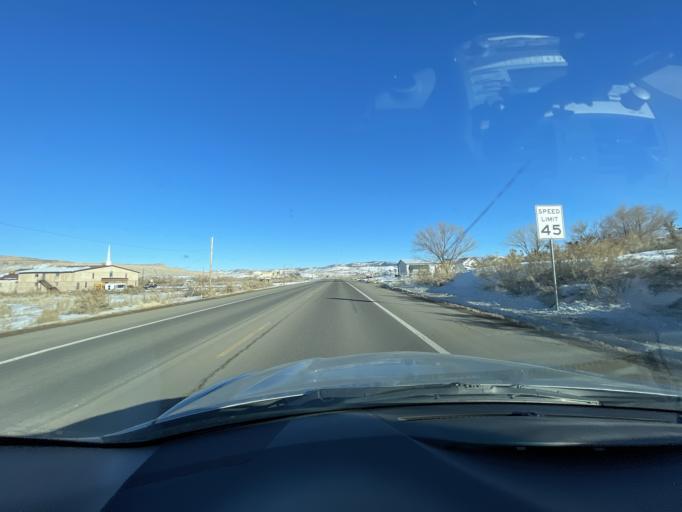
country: US
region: Colorado
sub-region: Rio Blanco County
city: Rangely
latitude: 40.0876
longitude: -108.7808
